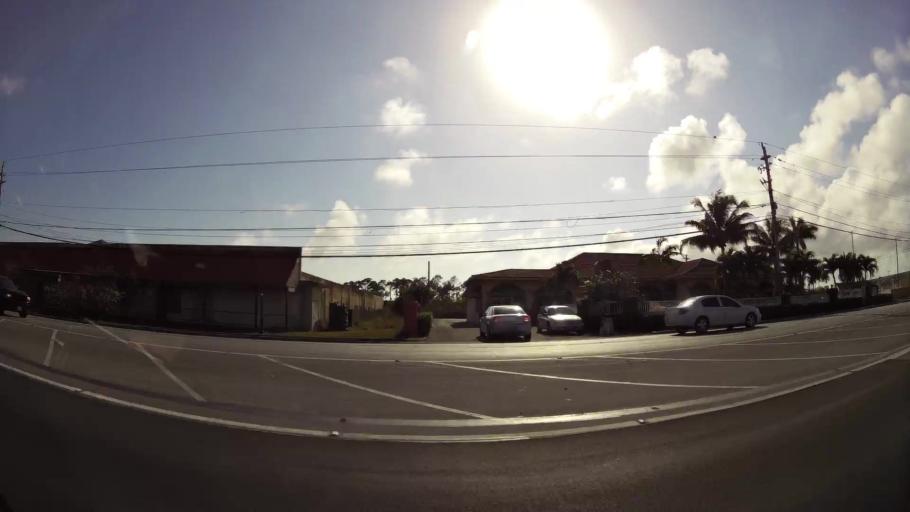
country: BS
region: Freeport
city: Lucaya
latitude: 26.5200
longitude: -78.6693
